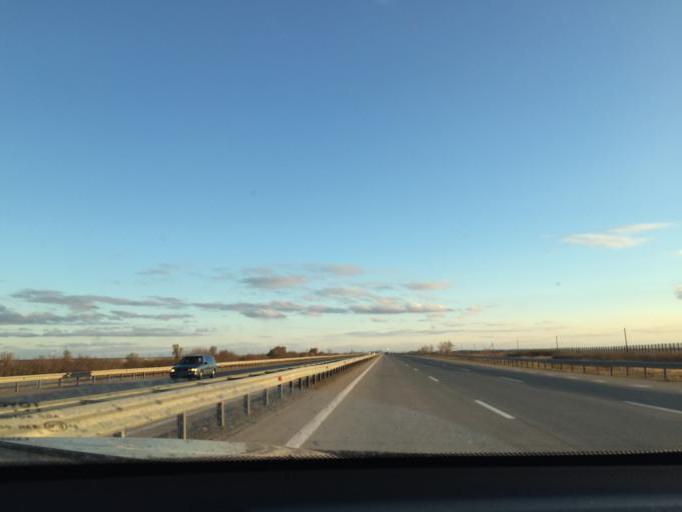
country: KZ
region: Astana Qalasy
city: Astana
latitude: 51.2873
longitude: 71.3607
